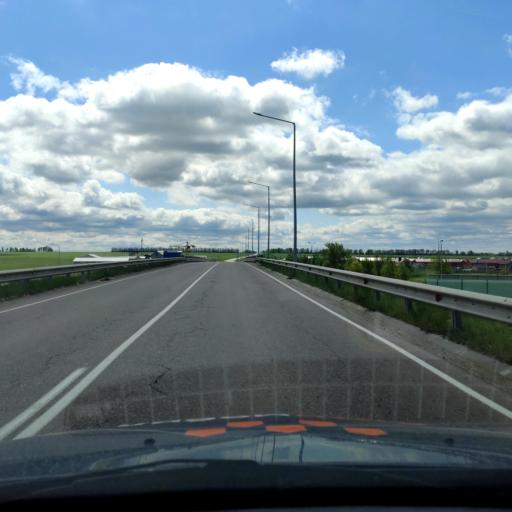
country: RU
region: Voronezj
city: Novaya Usman'
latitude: 51.6035
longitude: 39.3383
